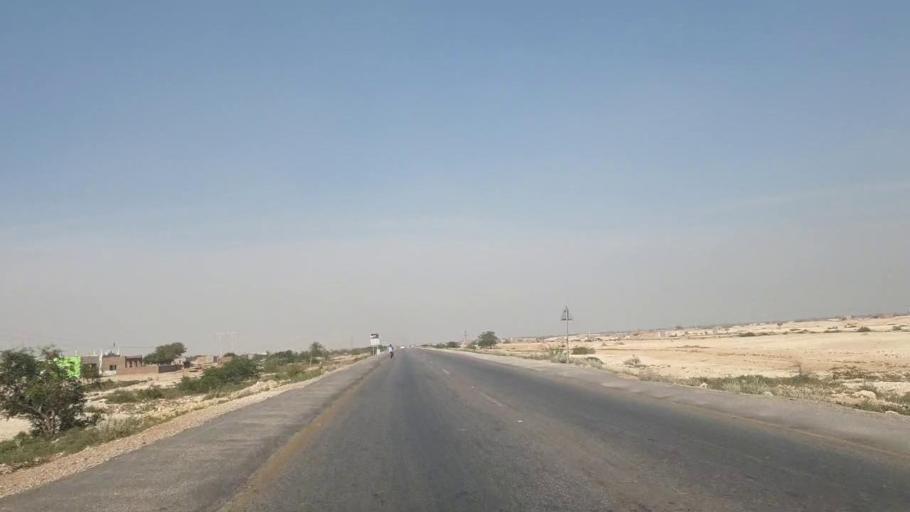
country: PK
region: Sindh
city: Hala
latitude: 25.8005
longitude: 68.2783
